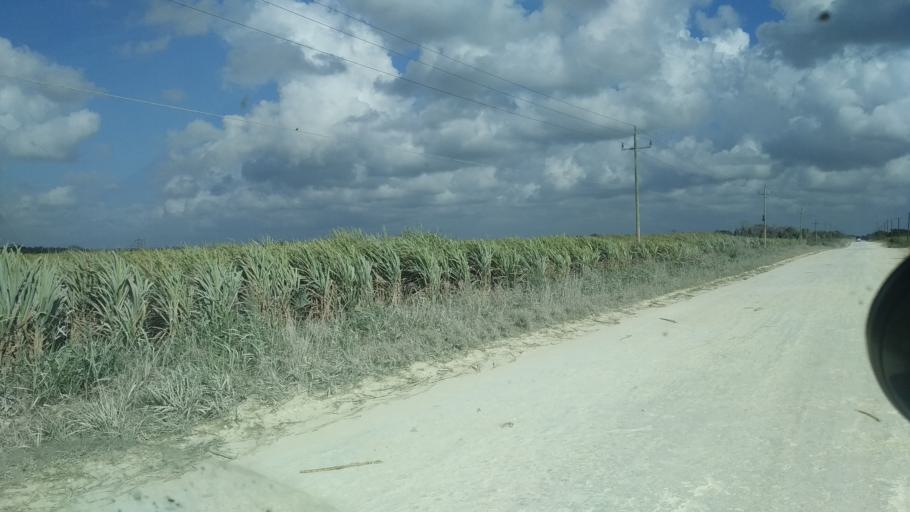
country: BZ
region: Corozal
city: Corozal
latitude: 18.3267
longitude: -88.4943
